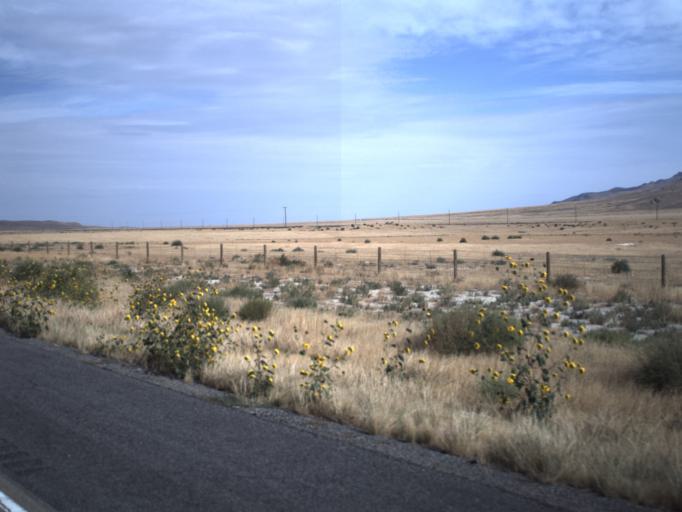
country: US
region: Utah
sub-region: Tooele County
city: Grantsville
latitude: 40.7952
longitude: -112.8403
